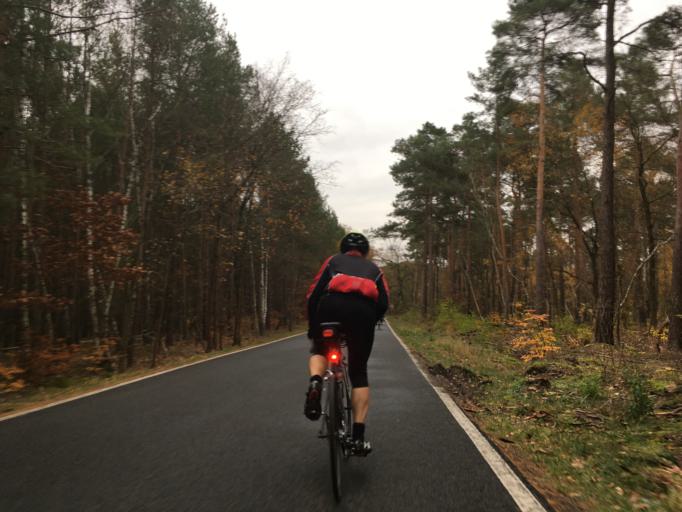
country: DE
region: Brandenburg
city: Gross Lindow
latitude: 52.2752
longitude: 14.4814
